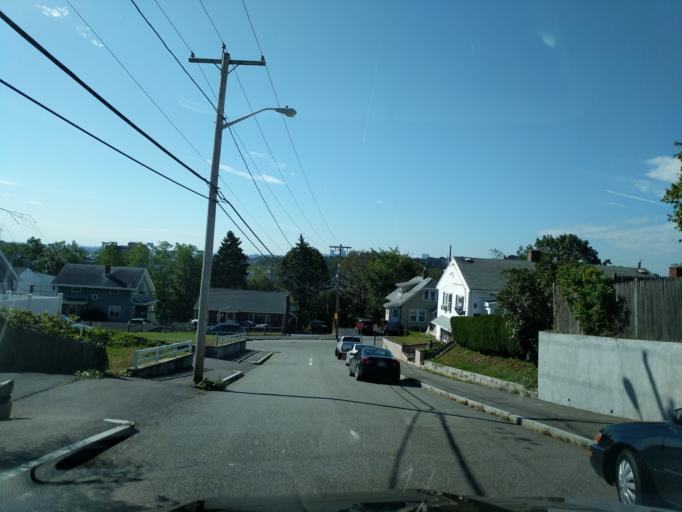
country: US
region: Massachusetts
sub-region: Suffolk County
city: Revere
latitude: 42.4079
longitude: -71.0207
